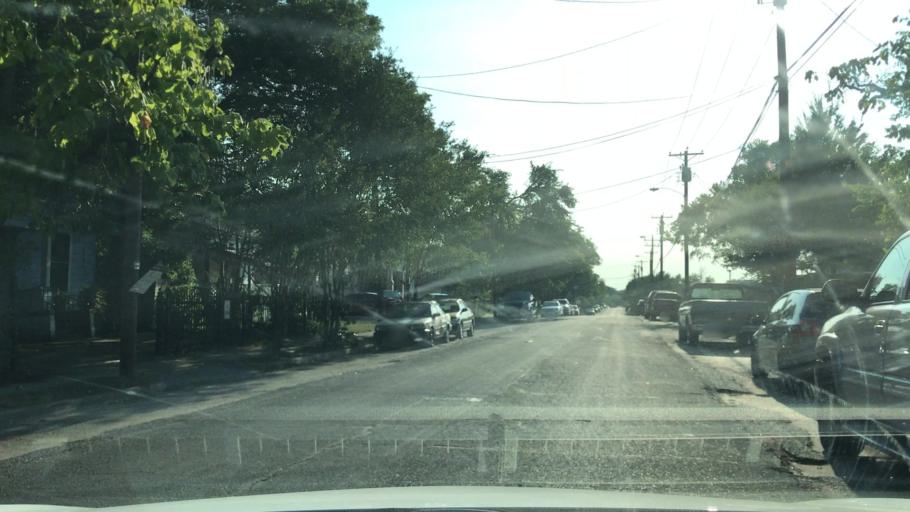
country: US
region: Texas
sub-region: Dallas County
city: Dallas
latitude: 32.7490
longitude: -96.8322
